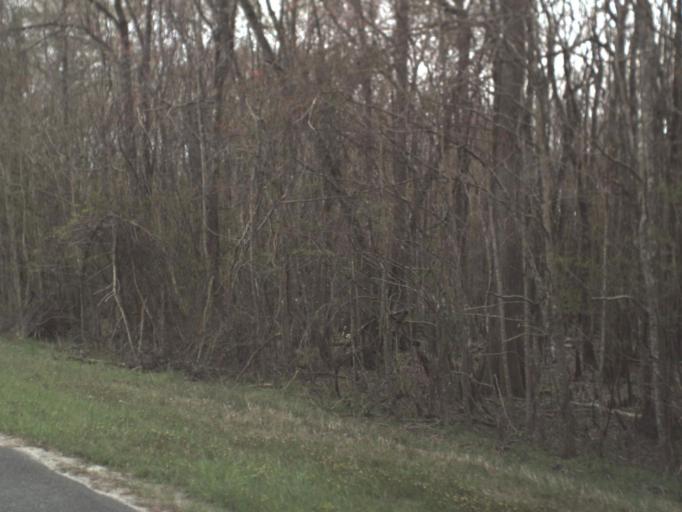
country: US
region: Florida
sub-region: Wakulla County
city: Crawfordville
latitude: 30.2464
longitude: -84.3169
